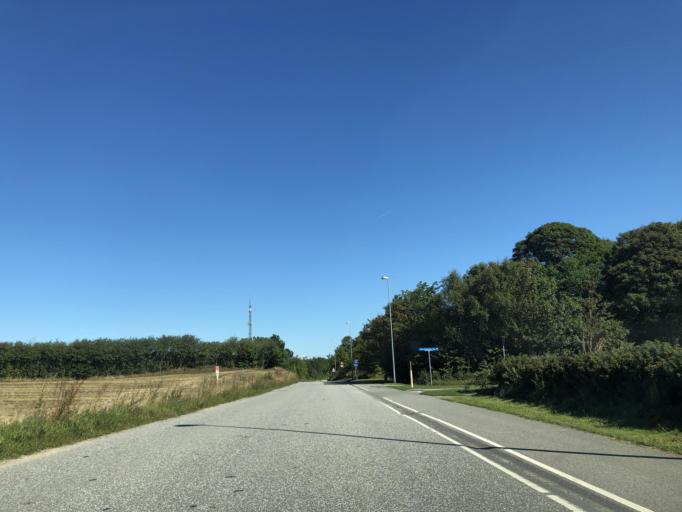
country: DK
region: North Denmark
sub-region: Mariagerfjord Kommune
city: Hobro
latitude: 56.6382
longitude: 9.7712
